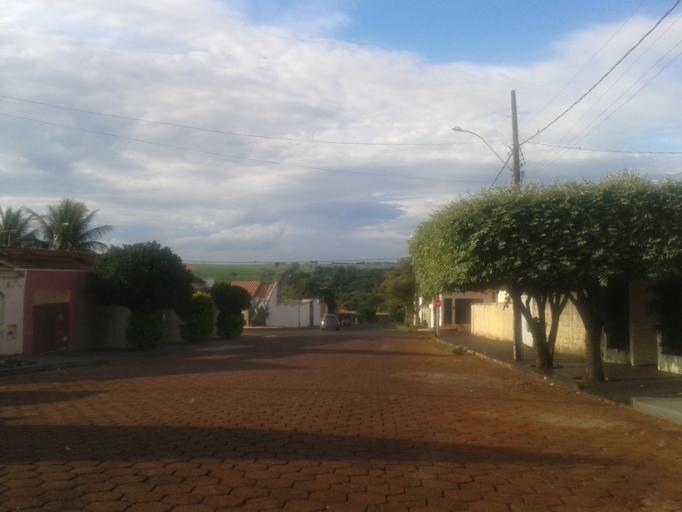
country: BR
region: Minas Gerais
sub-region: Capinopolis
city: Capinopolis
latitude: -18.6814
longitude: -49.5657
